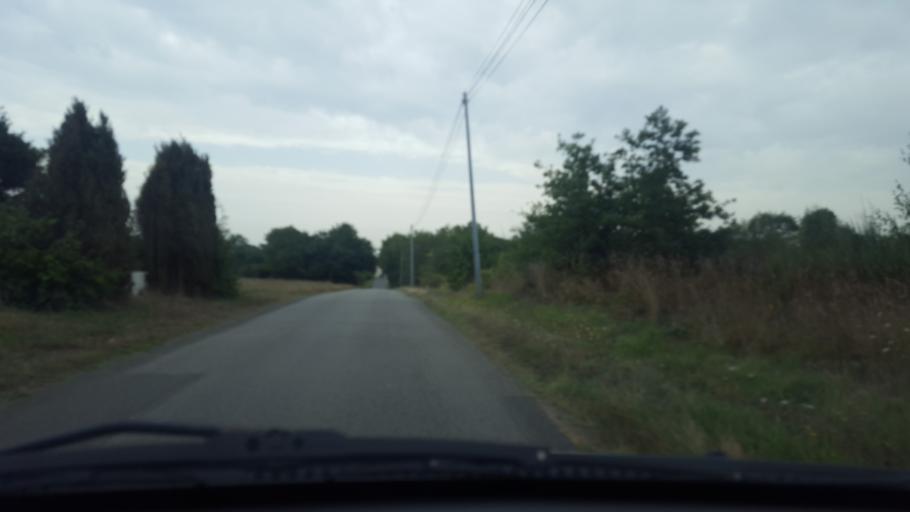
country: FR
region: Pays de la Loire
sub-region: Departement de la Loire-Atlantique
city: Saint-Philbert-de-Grand-Lieu
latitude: 47.0051
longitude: -1.6326
